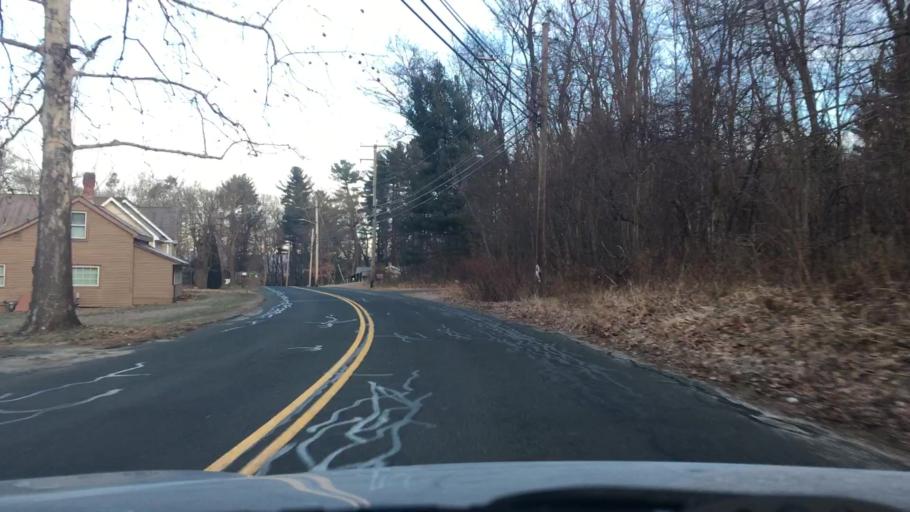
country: US
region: Massachusetts
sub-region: Hampden County
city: Westfield
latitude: 42.0942
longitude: -72.7109
